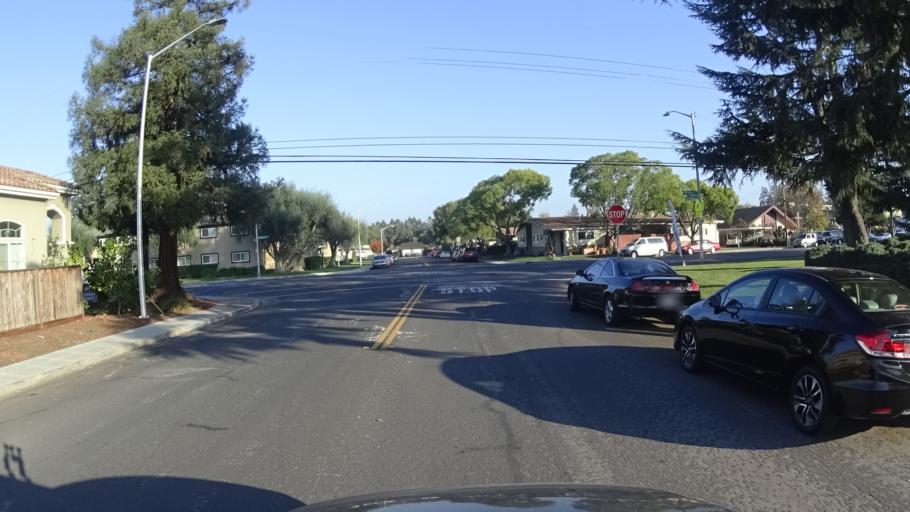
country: US
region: California
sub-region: Santa Clara County
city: Santa Clara
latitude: 37.3417
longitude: -121.9881
